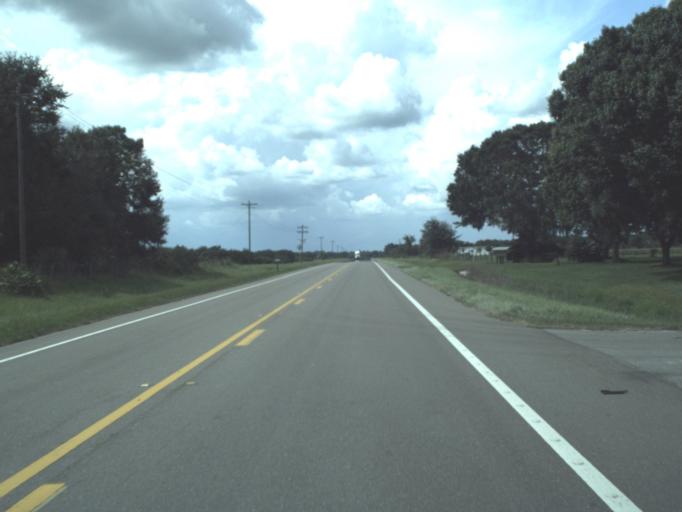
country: US
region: Florida
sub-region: Hardee County
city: Zolfo Springs
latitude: 27.4644
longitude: -81.7017
